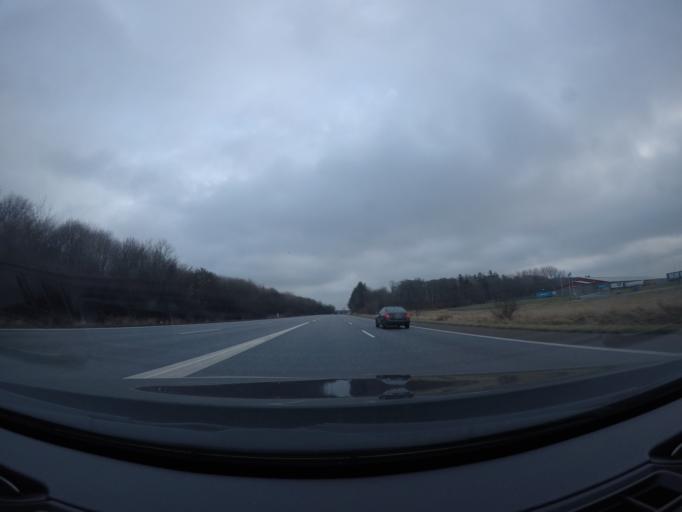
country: DK
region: South Denmark
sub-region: Fredericia Kommune
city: Taulov
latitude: 55.5387
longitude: 9.6681
